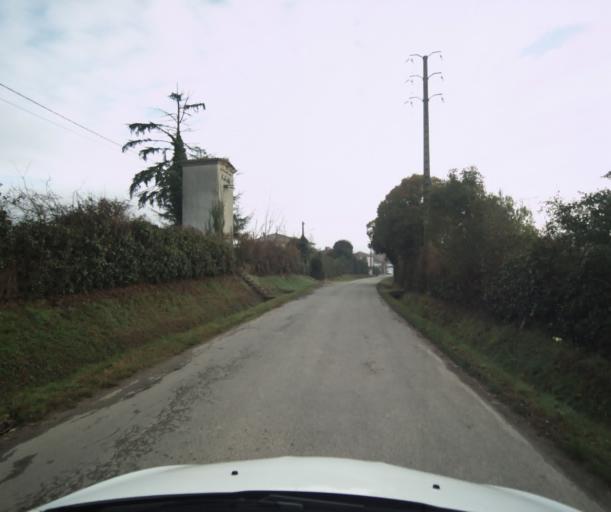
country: FR
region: Midi-Pyrenees
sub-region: Departement du Tarn-et-Garonne
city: Castelsarrasin
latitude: 44.0373
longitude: 1.1004
